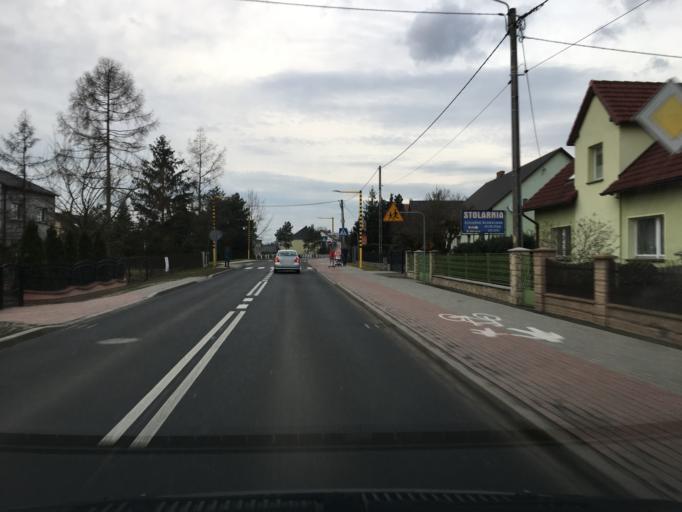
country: PL
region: Opole Voivodeship
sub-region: Powiat krapkowicki
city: Januszkowice
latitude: 50.3927
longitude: 18.1346
